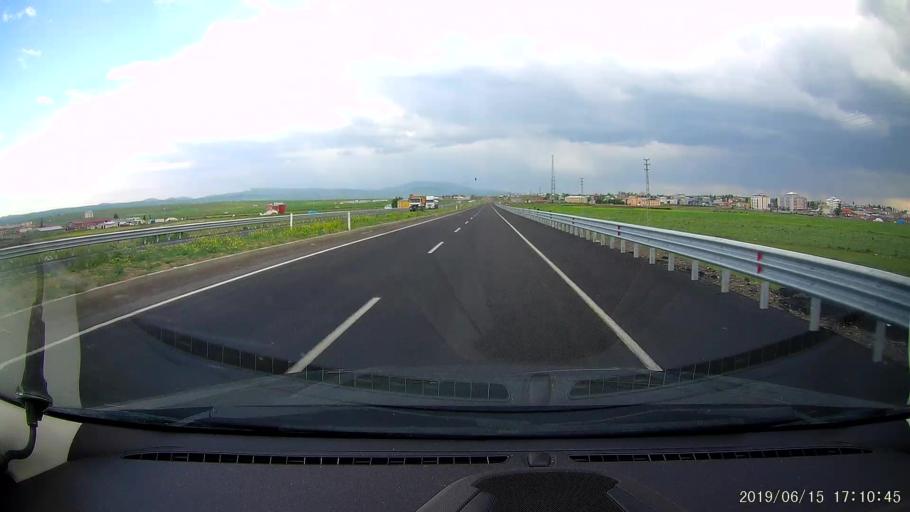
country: TR
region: Kars
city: Kars
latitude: 40.6187
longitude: 43.1335
